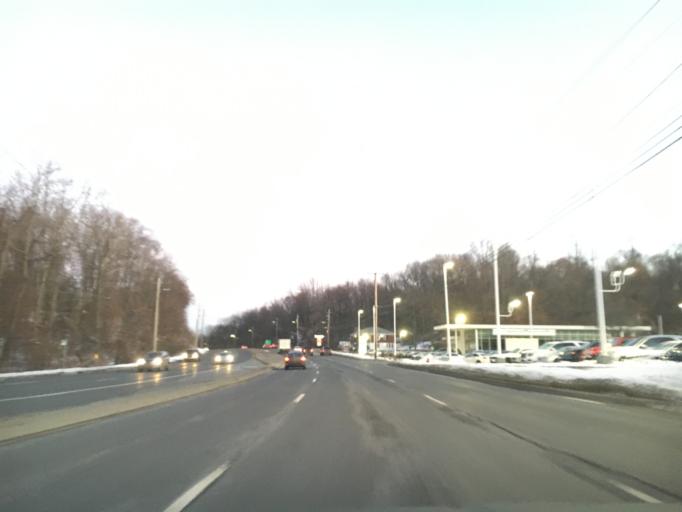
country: US
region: New York
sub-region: Dutchess County
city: Crown Heights
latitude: 41.6301
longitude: -73.9159
